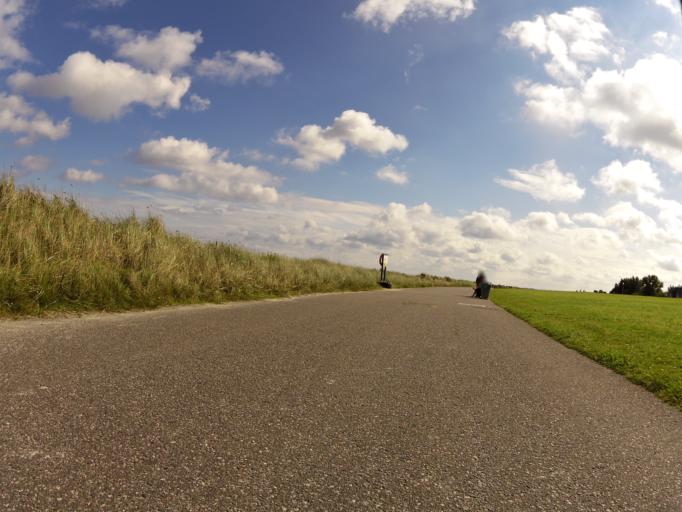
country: DE
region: Schleswig-Holstein
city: Wisch
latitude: 54.4259
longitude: 10.3874
